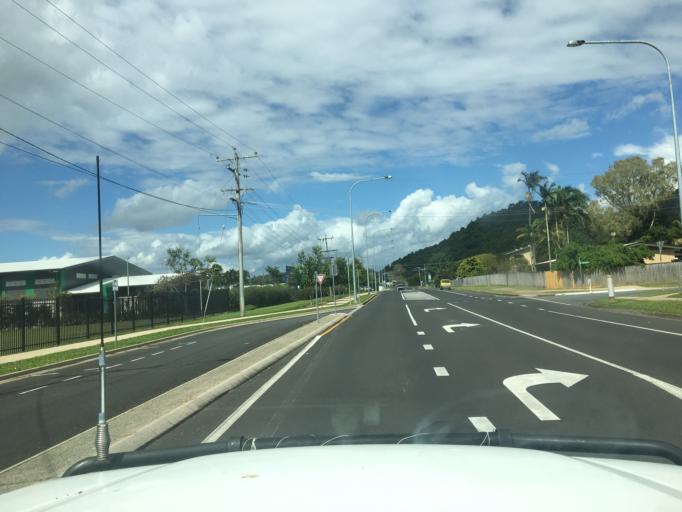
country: AU
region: Queensland
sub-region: Cairns
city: Woree
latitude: -16.9617
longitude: 145.7402
